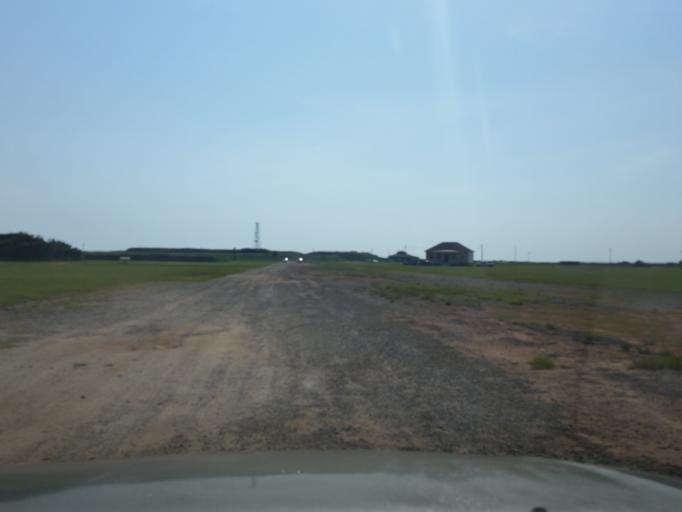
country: US
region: Alabama
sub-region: Mobile County
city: Dauphin Island
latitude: 30.2296
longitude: -88.0168
